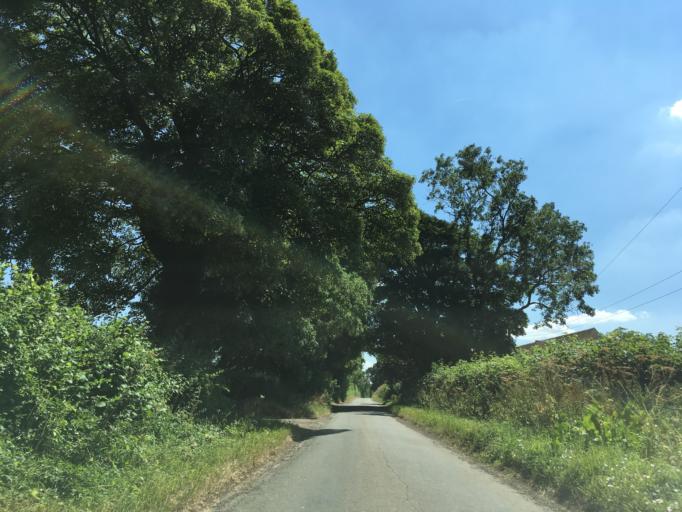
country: GB
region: England
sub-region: Gloucestershire
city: Tetbury
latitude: 51.6449
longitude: -2.1326
